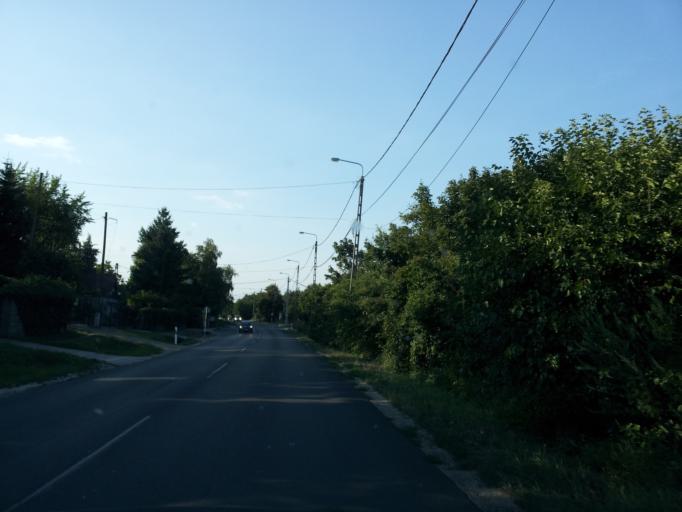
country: HU
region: Pest
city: Tahitotfalu
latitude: 47.7363
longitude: 19.0881
